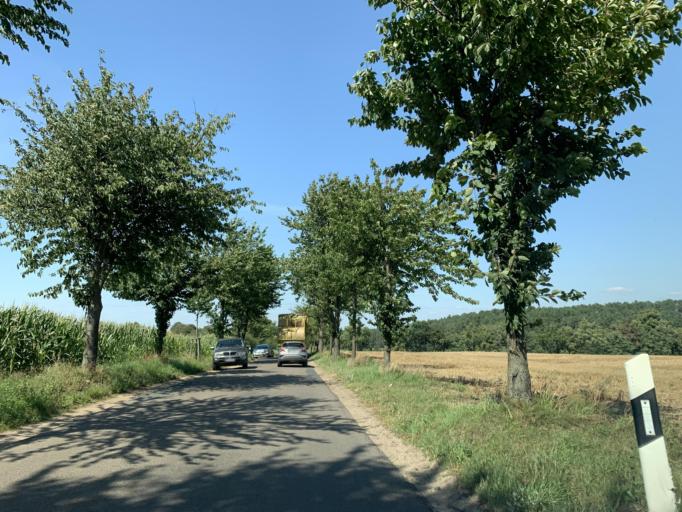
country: DE
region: Mecklenburg-Vorpommern
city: Loitz
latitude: 53.3624
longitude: 13.3863
